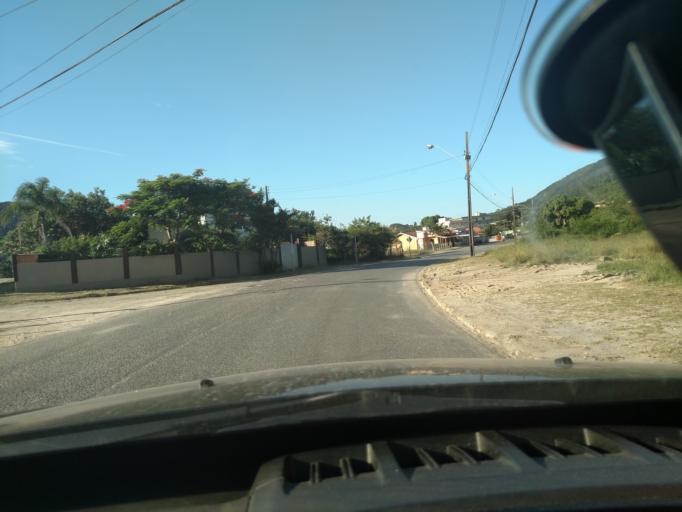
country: BR
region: Santa Catarina
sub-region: Porto Belo
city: Porto Belo
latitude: -27.1758
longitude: -48.5239
